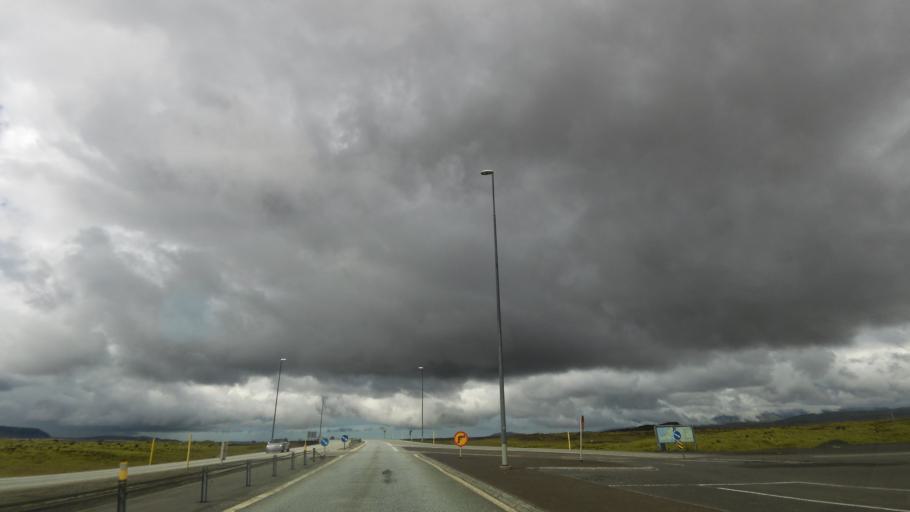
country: IS
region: Capital Region
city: Mosfellsbaer
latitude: 64.0575
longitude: -21.5018
